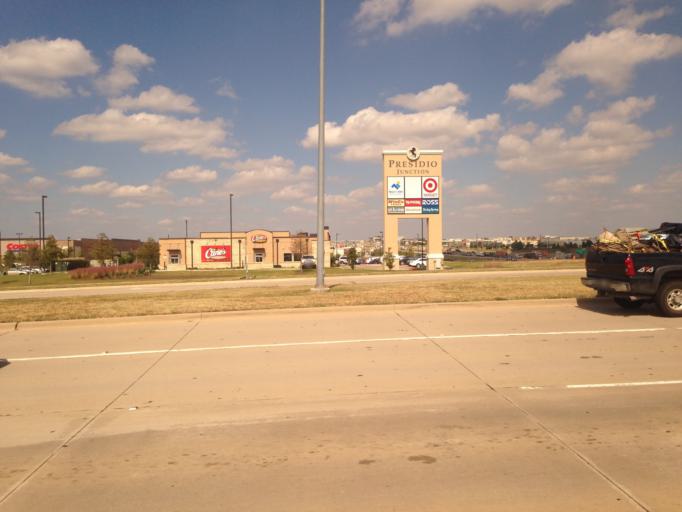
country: US
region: Texas
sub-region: Tarrant County
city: Blue Mound
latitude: 32.8983
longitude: -97.3188
